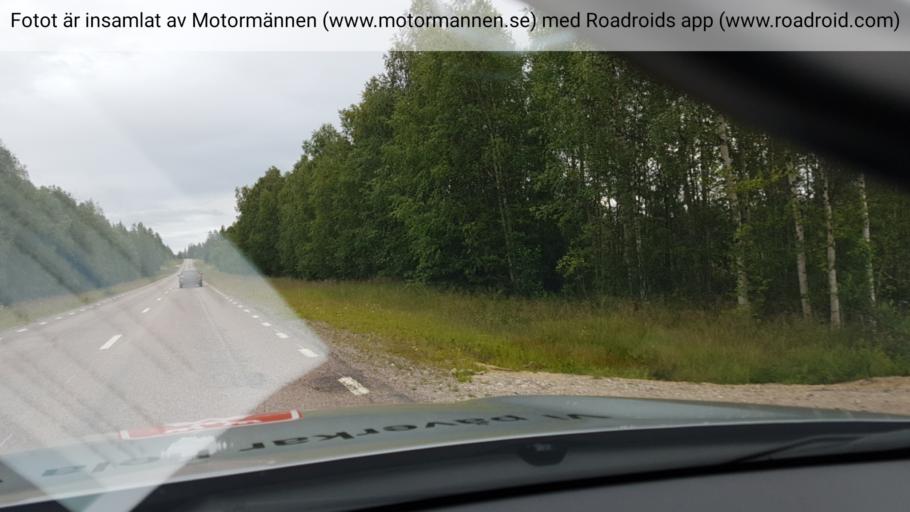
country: SE
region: Norrbotten
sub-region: Gallivare Kommun
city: Gaellivare
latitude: 67.0515
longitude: 21.6015
